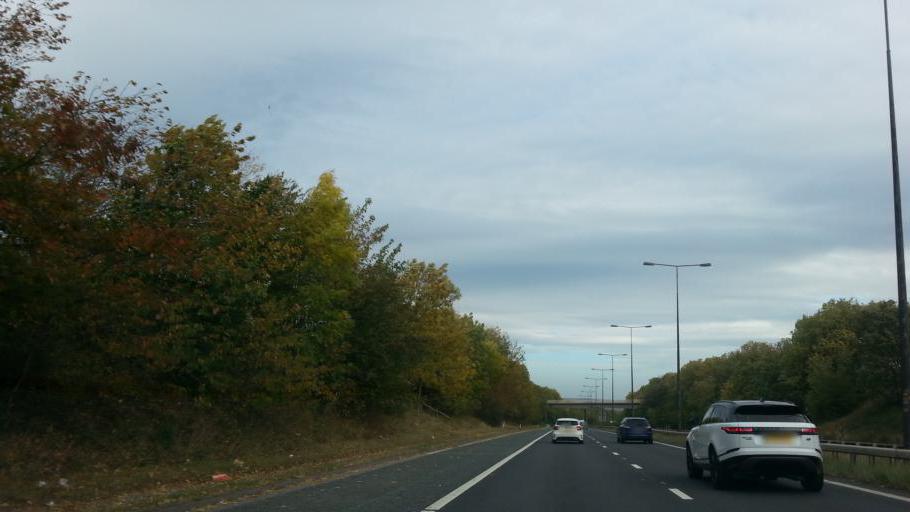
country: GB
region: England
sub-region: City and Borough of Leeds
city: Gildersome
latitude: 53.7517
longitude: -1.6169
